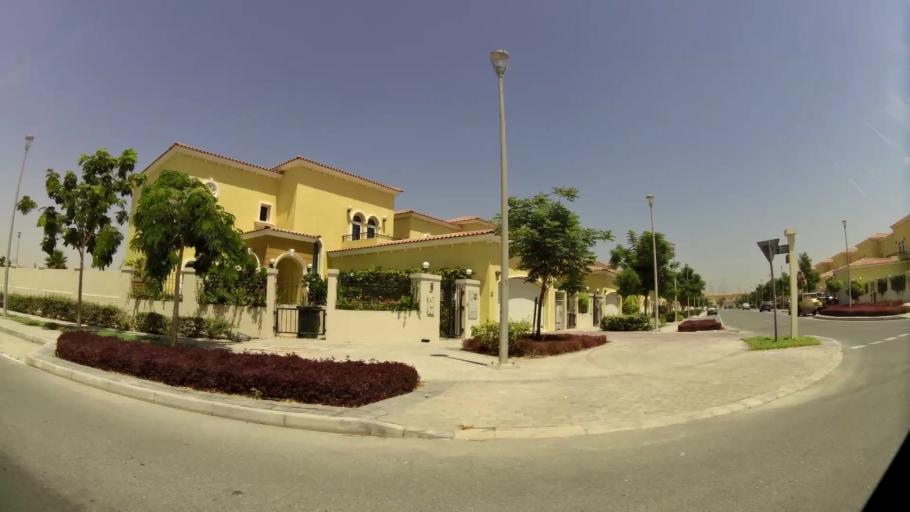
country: AE
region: Dubai
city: Dubai
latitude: 25.0357
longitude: 55.1676
